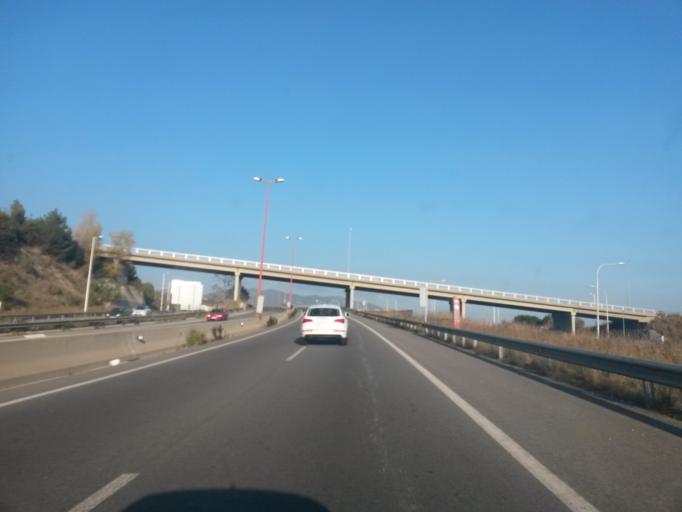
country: ES
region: Catalonia
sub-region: Provincia de Barcelona
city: Montgat
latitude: 41.4725
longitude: 2.2811
